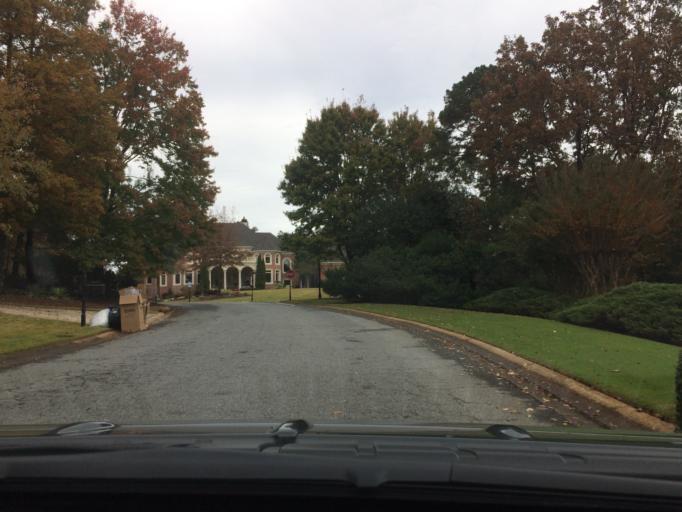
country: US
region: Georgia
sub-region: Fulton County
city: Johns Creek
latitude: 34.0031
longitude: -84.2501
